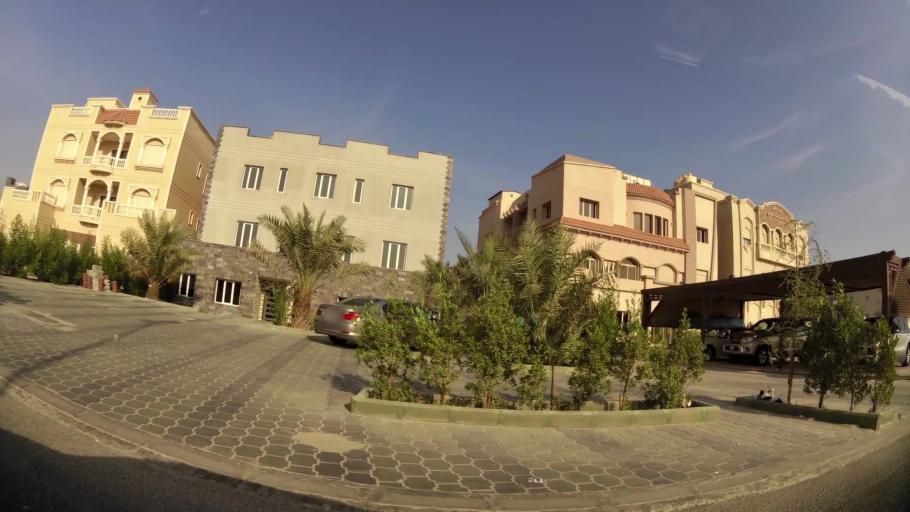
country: KW
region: Mubarak al Kabir
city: Mubarak al Kabir
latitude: 29.1834
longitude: 48.1019
